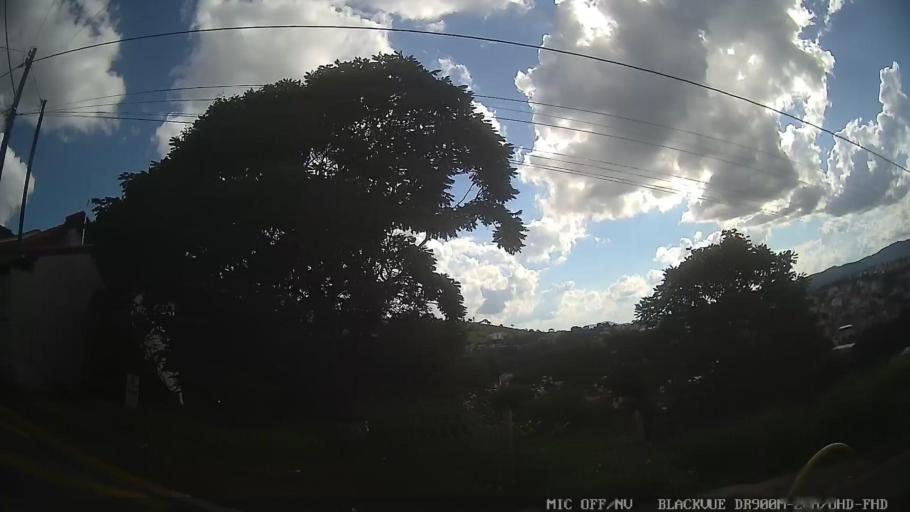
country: BR
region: Minas Gerais
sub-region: Extrema
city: Extrema
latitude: -22.8606
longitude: -46.3190
